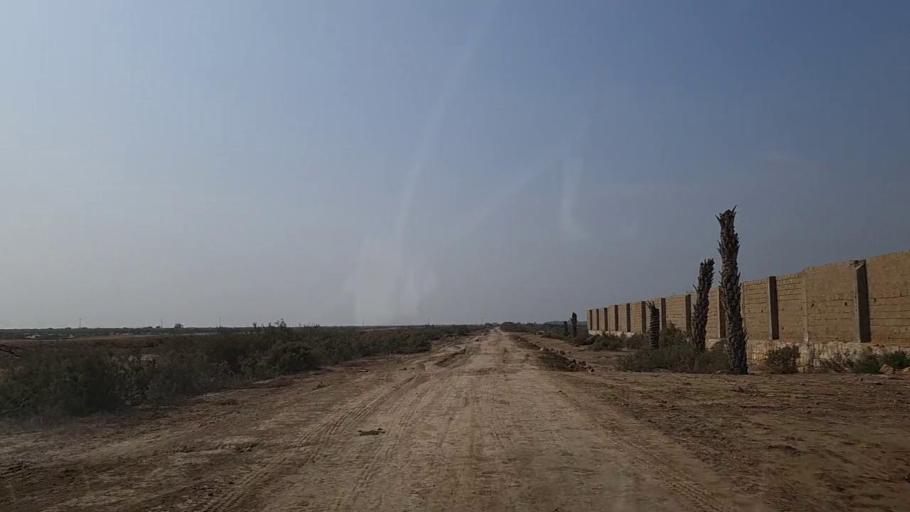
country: PK
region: Sindh
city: Gharo
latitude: 24.6735
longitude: 67.7099
